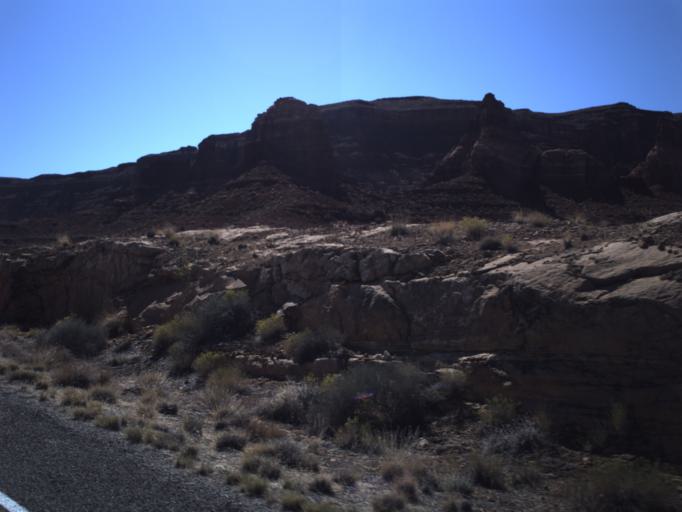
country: US
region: Utah
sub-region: San Juan County
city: Blanding
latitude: 37.8814
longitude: -110.3568
